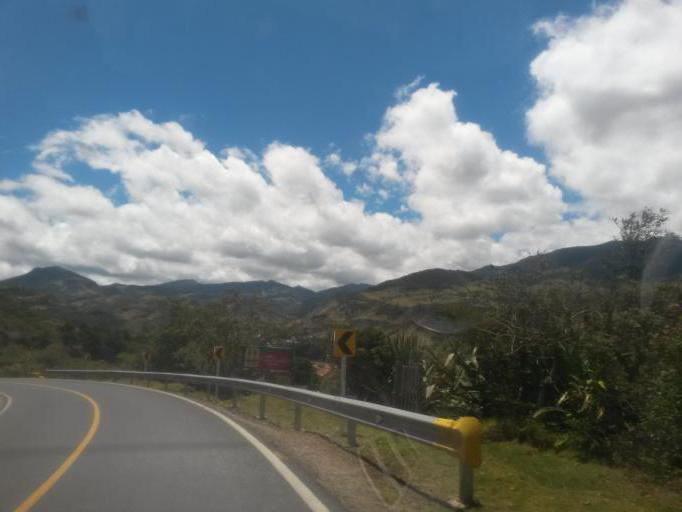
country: CO
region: Cauca
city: Silvia
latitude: 2.6038
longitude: -76.3923
